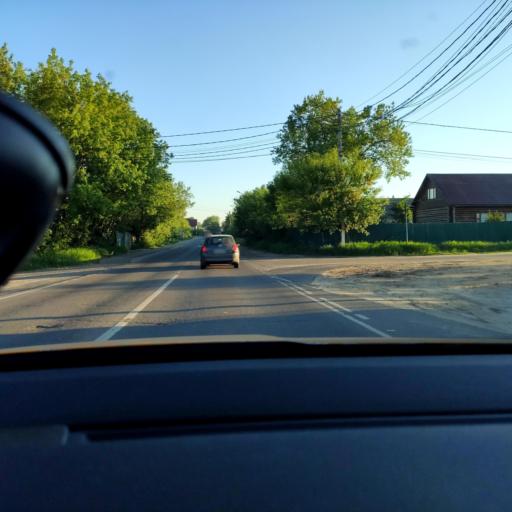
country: RU
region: Moskovskaya
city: Ramenskoye
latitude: 55.5543
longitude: 38.2326
